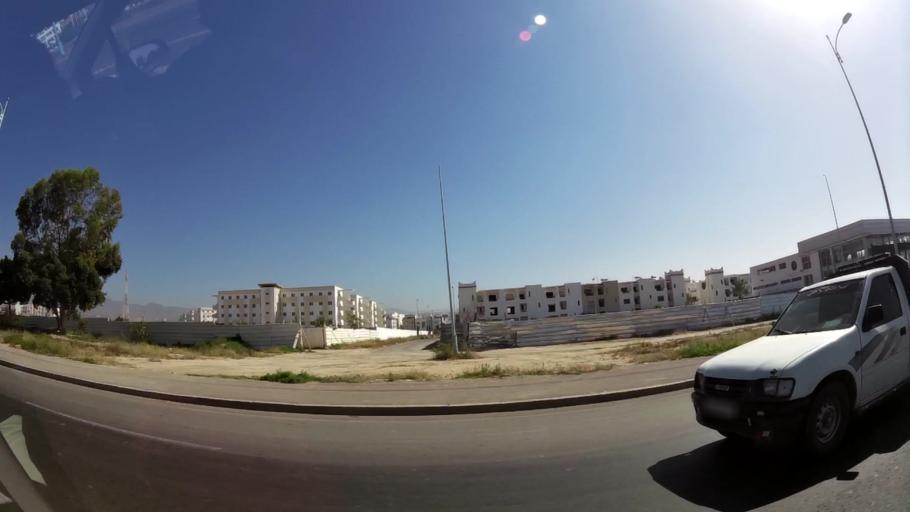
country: MA
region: Oued ed Dahab-Lagouira
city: Dakhla
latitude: 30.4002
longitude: -9.5272
